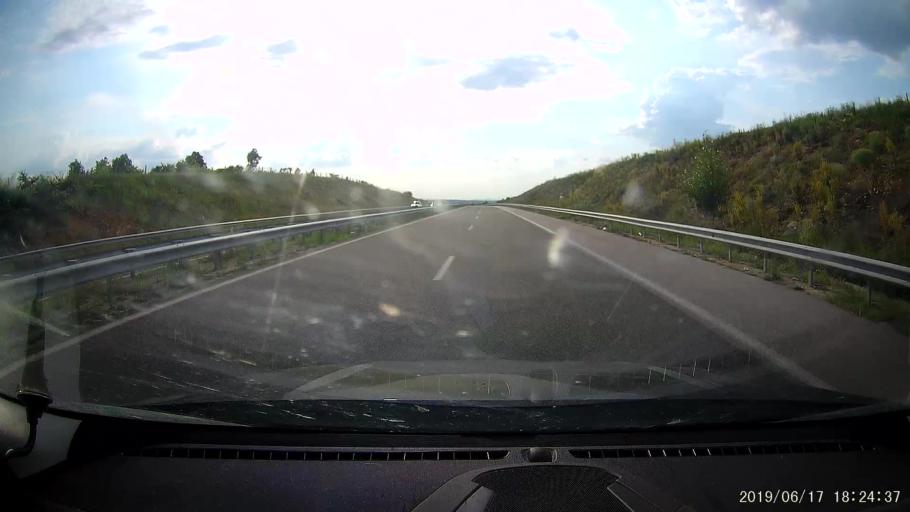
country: BG
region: Khaskovo
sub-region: Obshtina Dimitrovgrad
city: Dimitrovgrad
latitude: 41.9862
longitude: 25.6864
